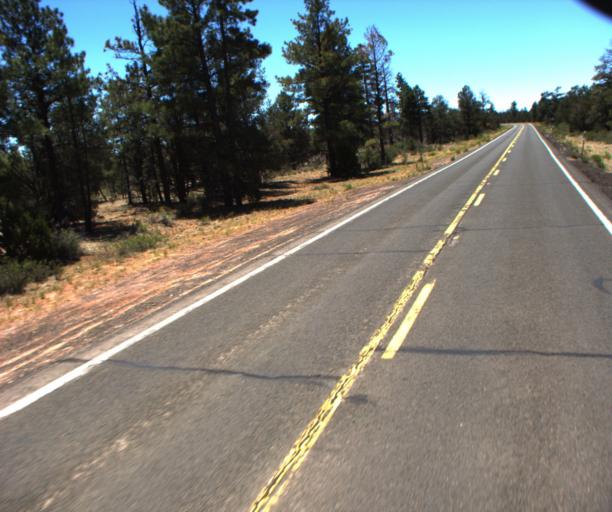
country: US
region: Arizona
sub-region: Gila County
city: Star Valley
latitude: 34.6940
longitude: -111.1081
